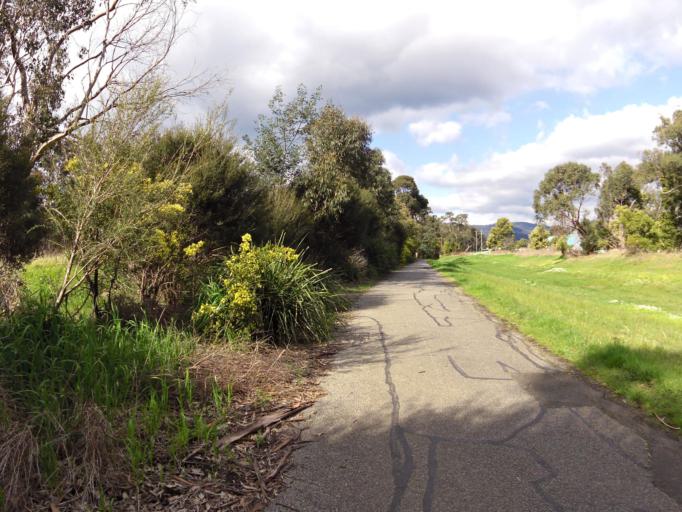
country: AU
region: Victoria
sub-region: Maroondah
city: Bayswater North
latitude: -37.8332
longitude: 145.2843
